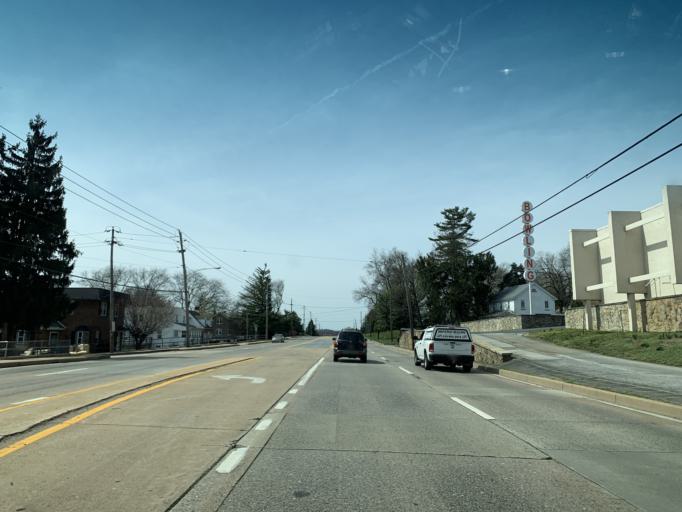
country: US
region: Delaware
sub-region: New Castle County
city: Newport
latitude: 39.7143
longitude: -75.6194
